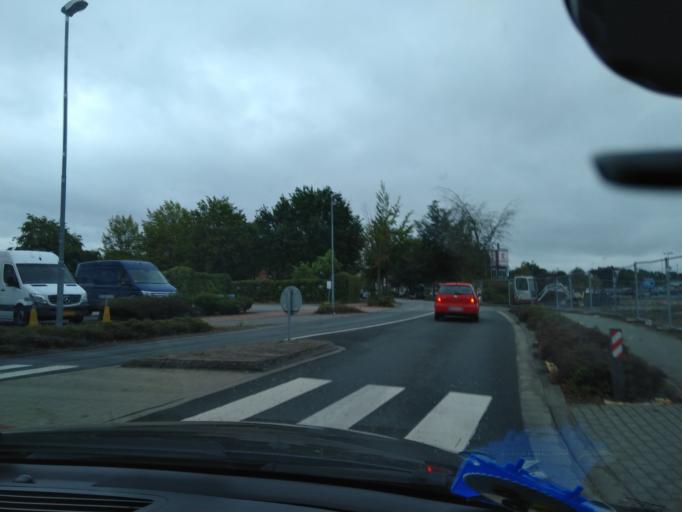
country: DE
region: Lower Saxony
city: Nordhorn
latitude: 52.4243
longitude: 7.0783
